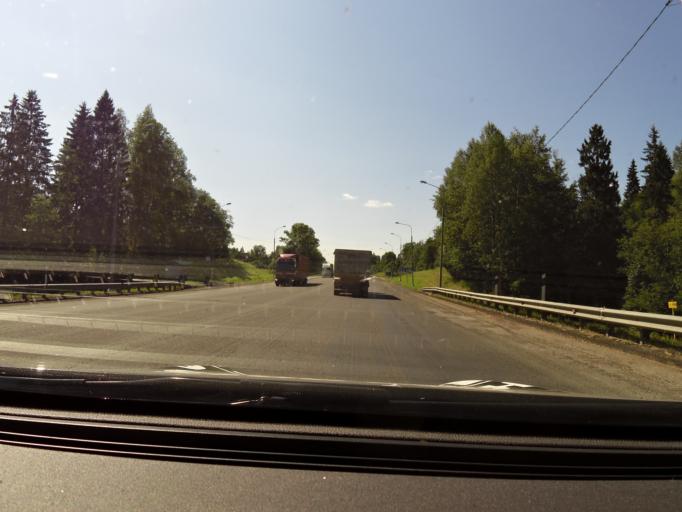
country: RU
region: Novgorod
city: Proletariy
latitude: 58.3672
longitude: 32.1019
